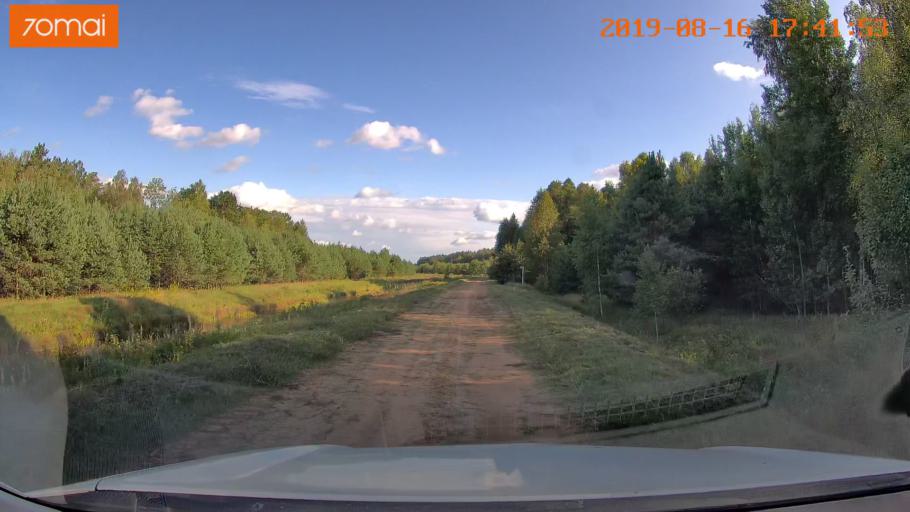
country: BY
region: Mogilev
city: Asipovichy
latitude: 53.2387
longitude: 28.6648
